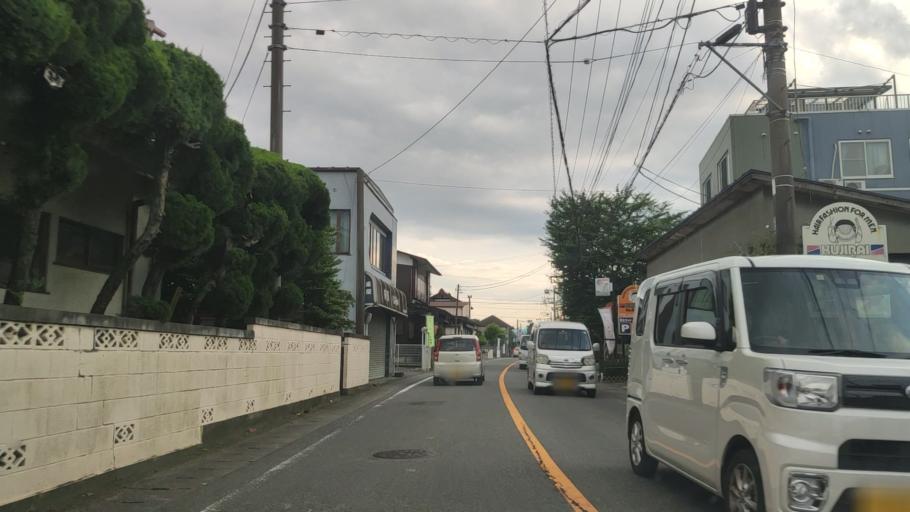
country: JP
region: Saitama
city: Hanno
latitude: 35.8040
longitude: 139.3068
